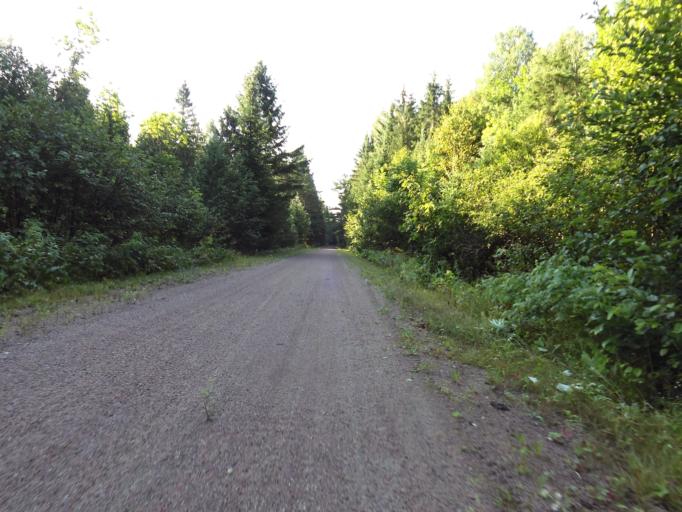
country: CA
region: Quebec
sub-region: Outaouais
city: Maniwaki
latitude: 46.2771
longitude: -76.0141
